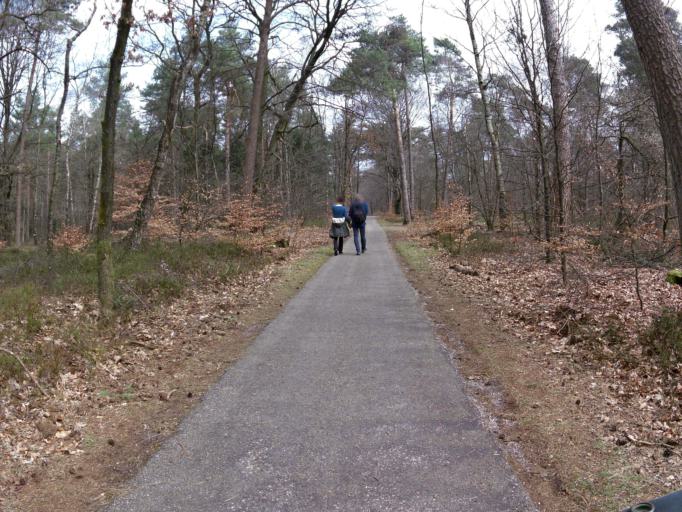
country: NL
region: Gelderland
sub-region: Gemeente Rozendaal
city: Rozendaal
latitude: 52.0164
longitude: 5.9731
